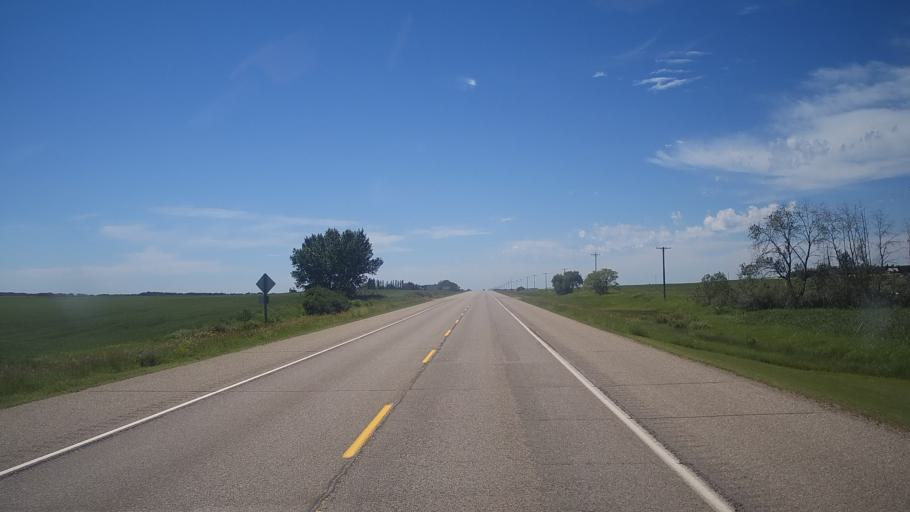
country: CA
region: Saskatchewan
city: Langenburg
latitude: 50.7714
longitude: -101.3107
